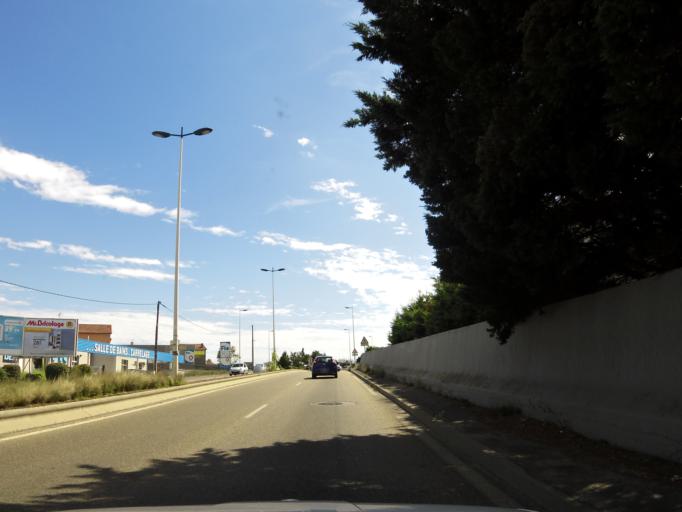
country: FR
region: Languedoc-Roussillon
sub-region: Departement du Gard
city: Ales
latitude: 44.1314
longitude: 4.1059
